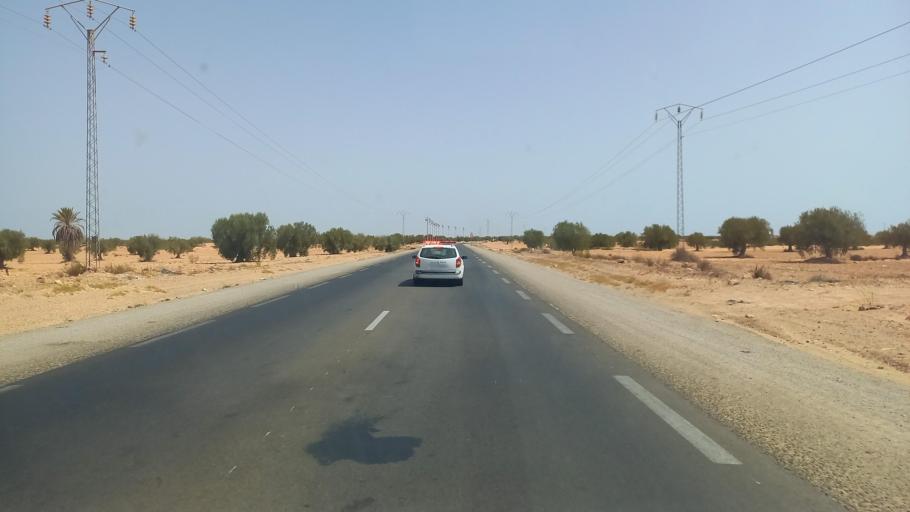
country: TN
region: Madanin
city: Zarzis
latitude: 33.4226
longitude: 10.8810
